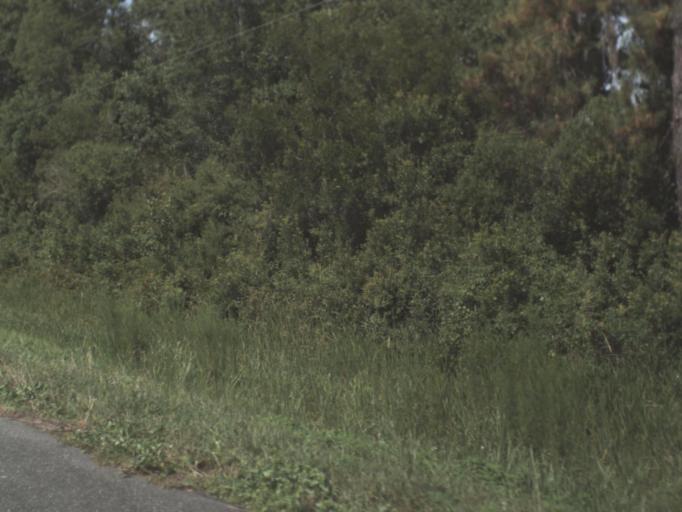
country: US
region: Florida
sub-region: Lafayette County
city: Mayo
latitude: 29.9914
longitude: -83.1970
